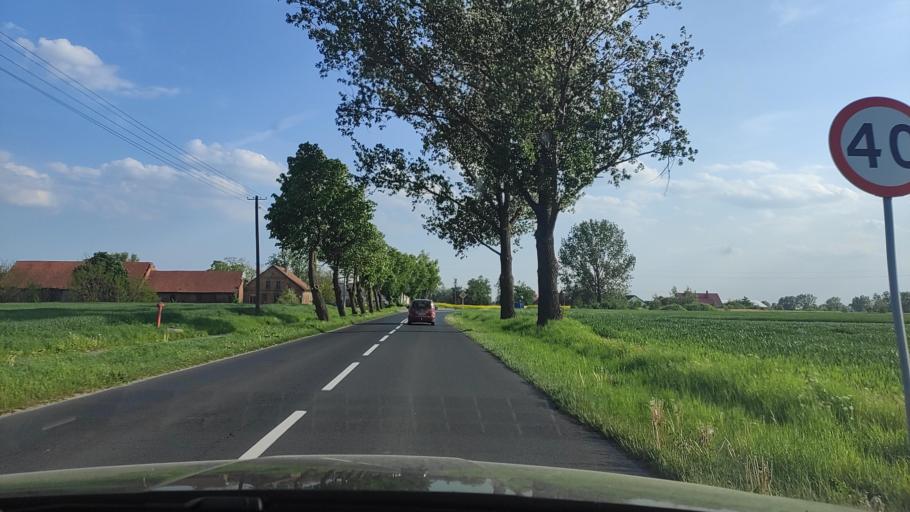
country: PL
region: Greater Poland Voivodeship
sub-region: Powiat poznanski
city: Kleszczewo
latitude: 52.3526
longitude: 17.1722
